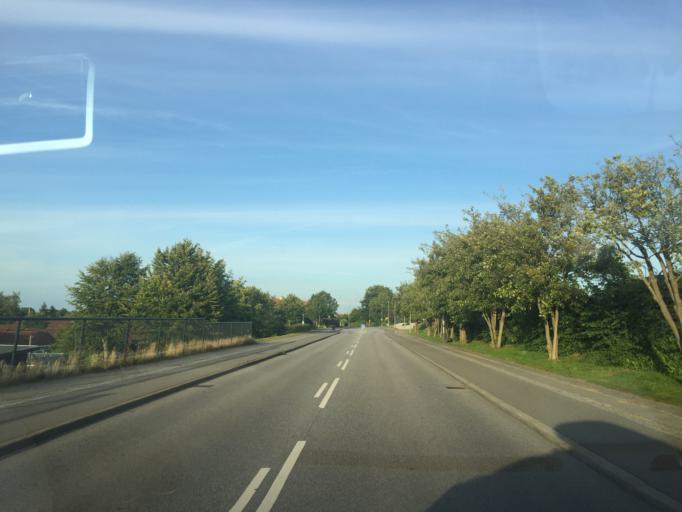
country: DK
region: South Denmark
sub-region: Kolding Kommune
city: Kolding
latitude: 55.4778
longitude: 9.4997
